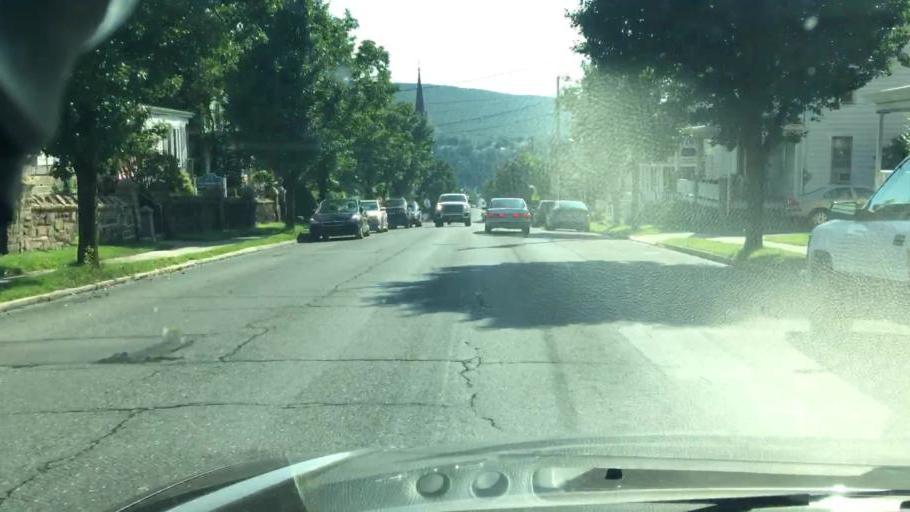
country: US
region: Pennsylvania
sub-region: Carbon County
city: Jim Thorpe
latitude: 40.8773
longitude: -75.7305
